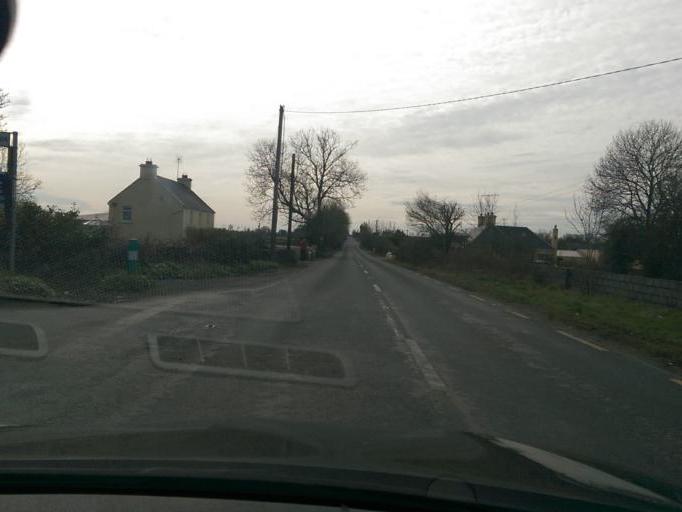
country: IE
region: Connaught
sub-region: County Galway
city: Claregalway
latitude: 53.3909
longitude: -8.8428
